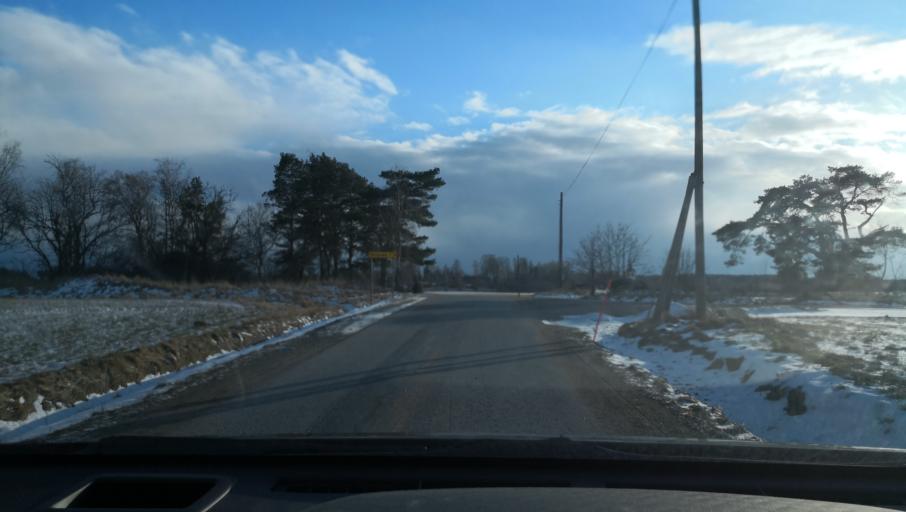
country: SE
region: Uppsala
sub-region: Enkopings Kommun
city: Irsta
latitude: 59.6880
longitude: 16.8579
